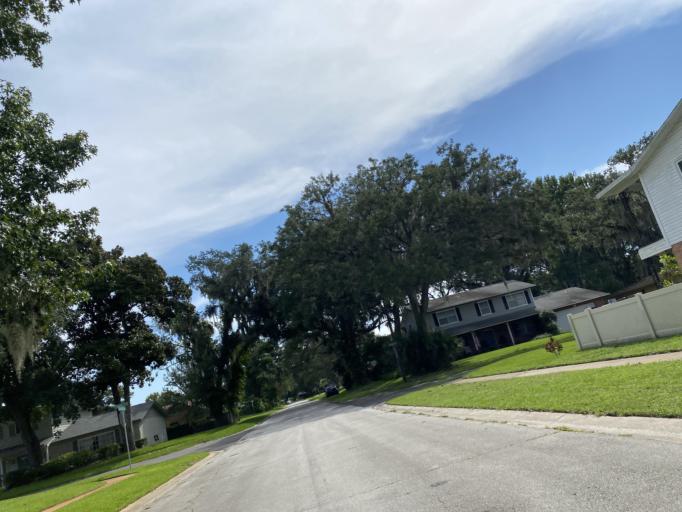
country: US
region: Florida
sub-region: Volusia County
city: Port Orange
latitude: 29.1342
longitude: -81.0050
